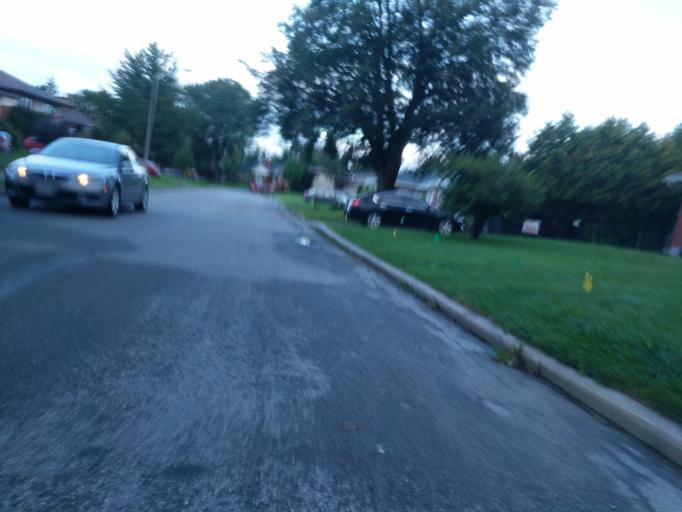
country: CA
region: Ontario
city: Ottawa
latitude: 45.3642
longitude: -75.7545
